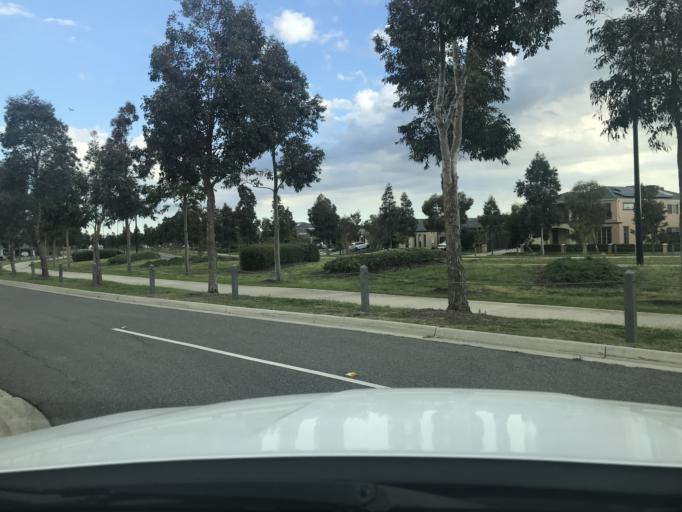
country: AU
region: Victoria
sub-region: Hume
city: Craigieburn
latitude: -37.5782
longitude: 144.9120
